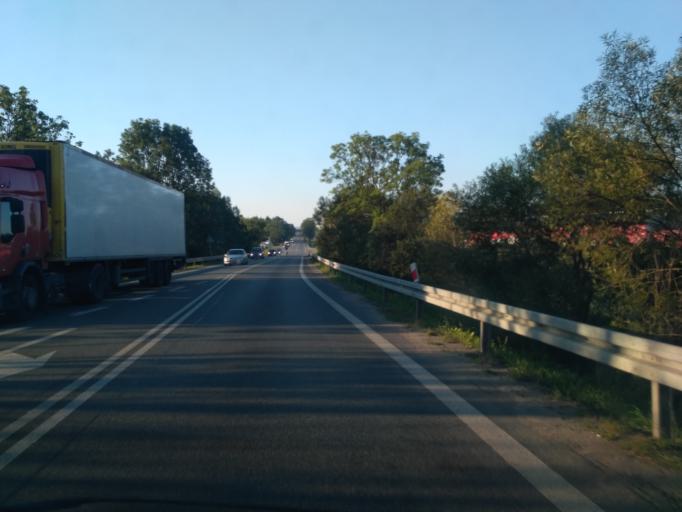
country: PL
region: Subcarpathian Voivodeship
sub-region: Krosno
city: Krosno
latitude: 49.6657
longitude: 21.7775
